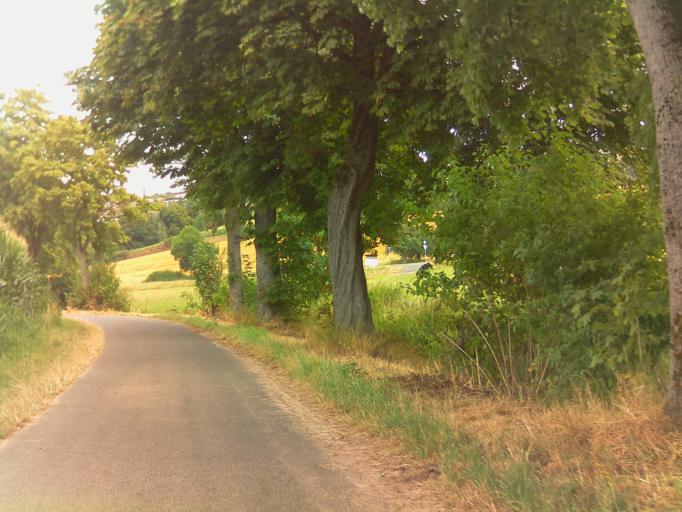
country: DE
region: Hesse
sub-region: Regierungsbezirk Darmstadt
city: Langenselbold
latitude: 50.2236
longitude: 9.0592
